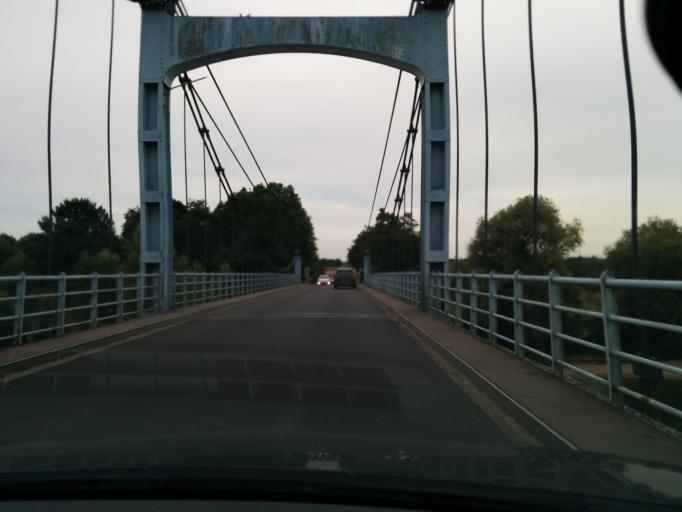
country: FR
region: Centre
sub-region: Departement du Loiret
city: Chateauneuf-sur-Loire
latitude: 47.8581
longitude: 2.2234
